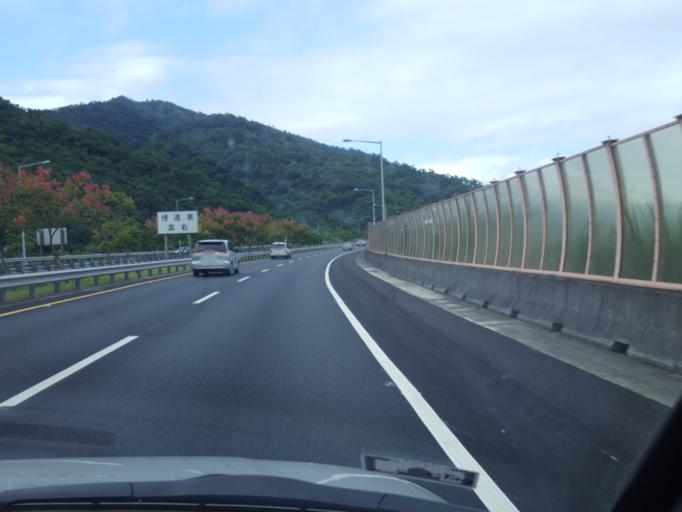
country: TW
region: Taiwan
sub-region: Yilan
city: Yilan
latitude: 24.8427
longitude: 121.7893
